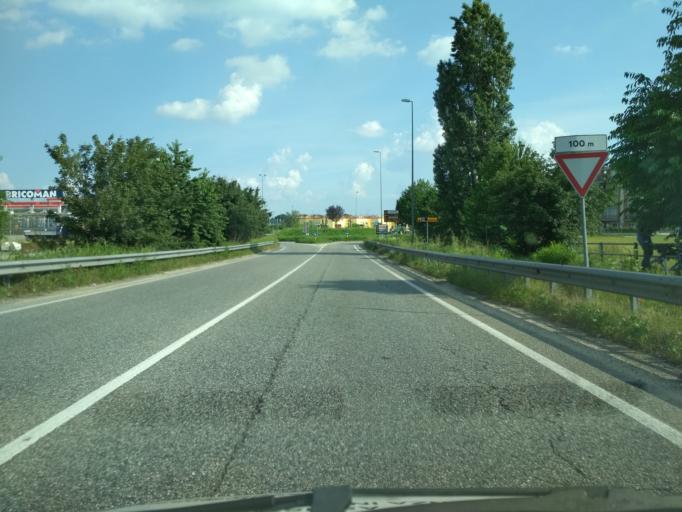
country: IT
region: Piedmont
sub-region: Provincia di Torino
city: Pasta
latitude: 45.0144
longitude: 7.5551
